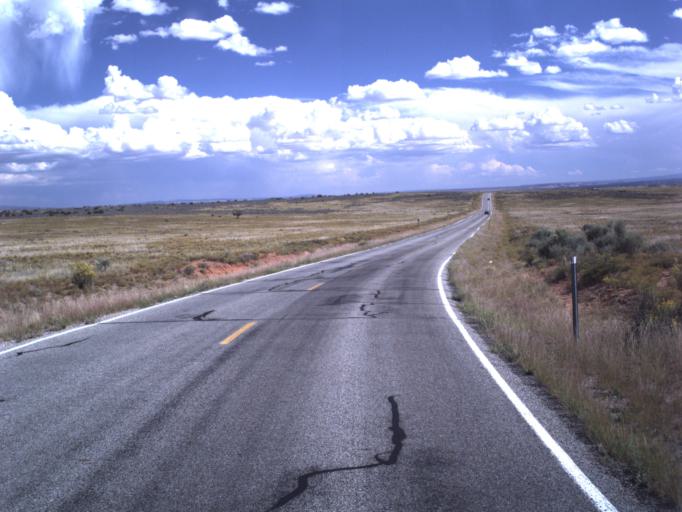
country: US
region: Utah
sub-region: Grand County
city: Moab
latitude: 38.5434
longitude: -109.7605
